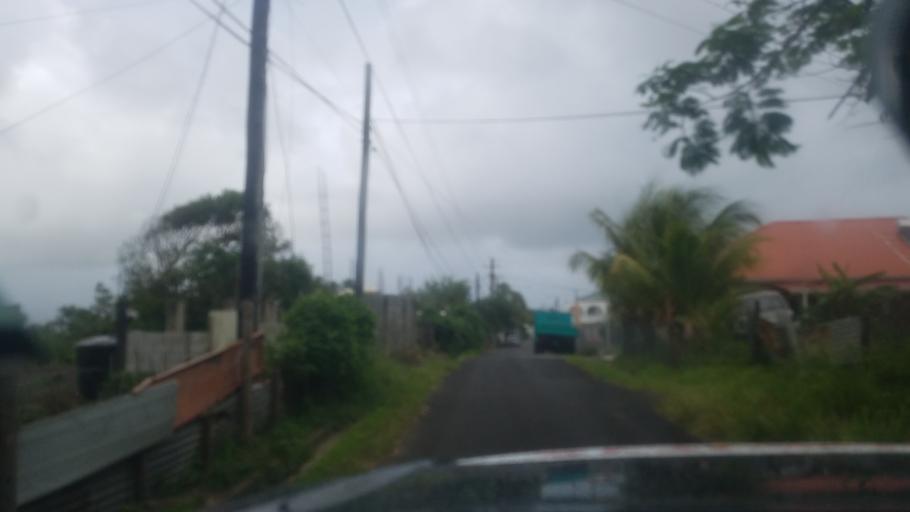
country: LC
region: Laborie Quarter
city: Laborie
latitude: 13.7648
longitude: -60.9758
